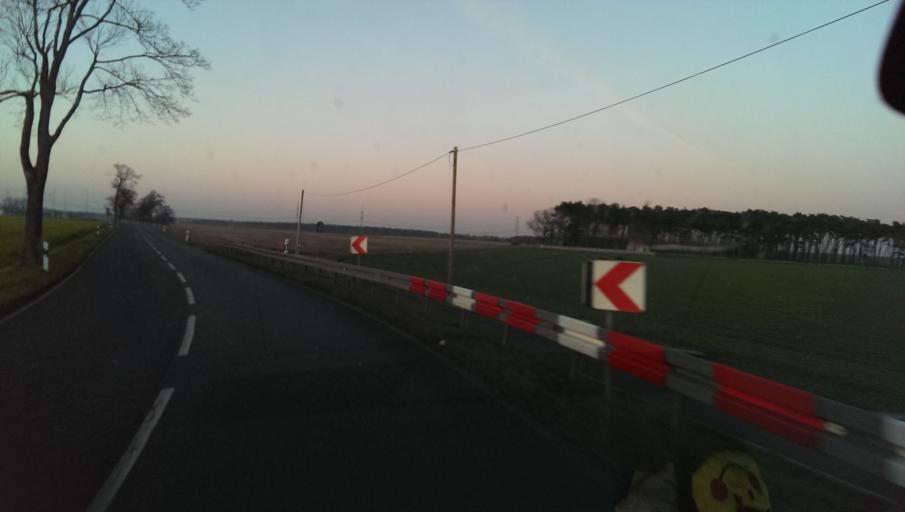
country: DE
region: Saxony-Anhalt
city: Holzdorf
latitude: 51.8206
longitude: 13.1663
